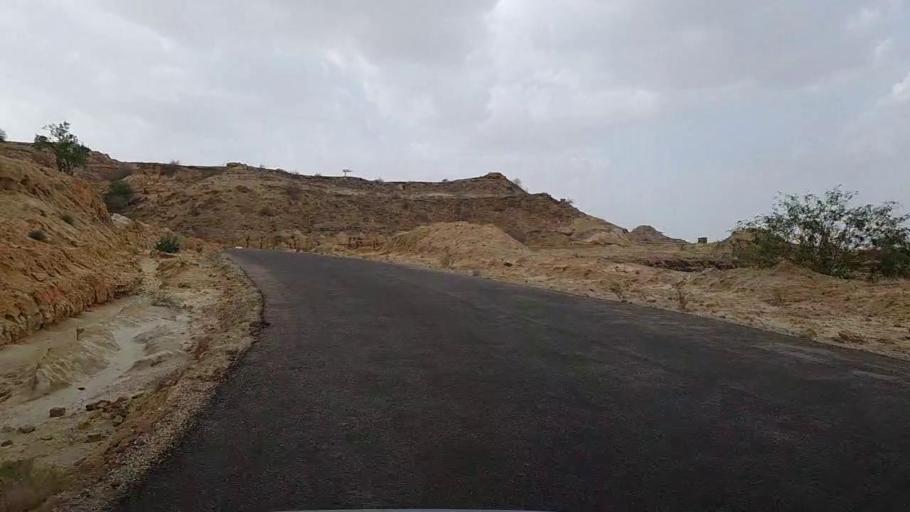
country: PK
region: Sindh
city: Jamshoro
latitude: 25.4250
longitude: 67.6914
